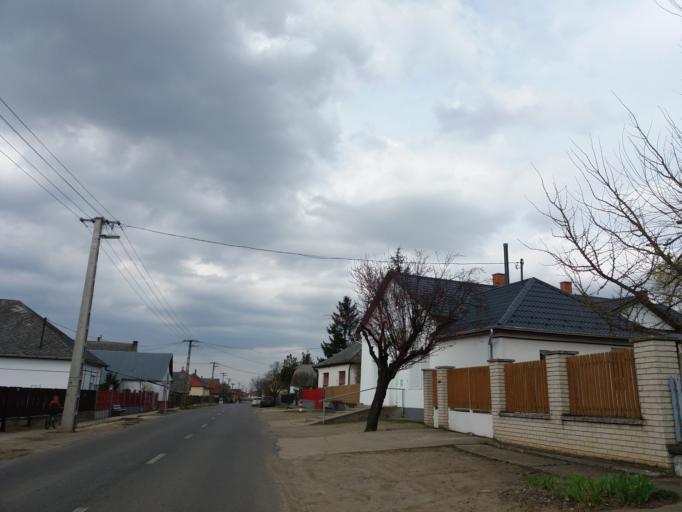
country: HU
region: Szabolcs-Szatmar-Bereg
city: Nyirtass
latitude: 48.1132
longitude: 22.0218
